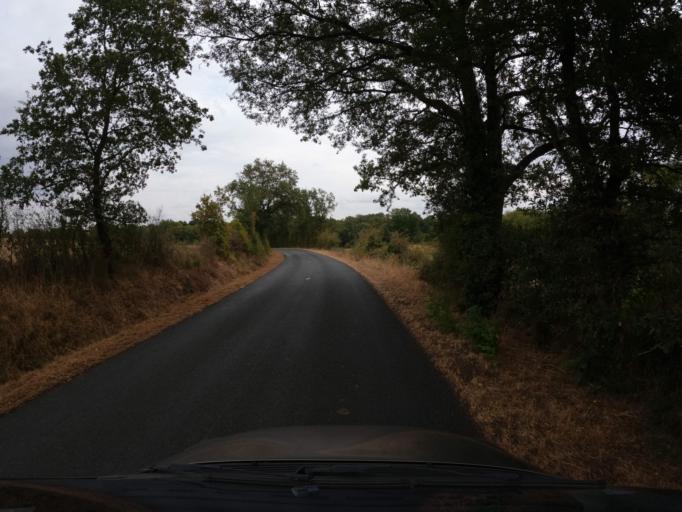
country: FR
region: Pays de la Loire
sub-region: Departement de la Vendee
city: Tiffauges
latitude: 46.9941
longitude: -1.1105
